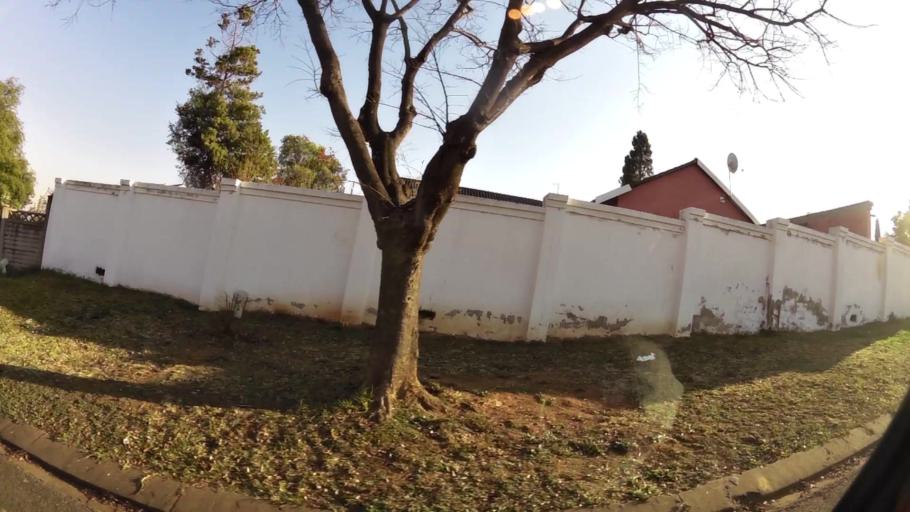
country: ZA
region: Gauteng
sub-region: City of Johannesburg Metropolitan Municipality
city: Soweto
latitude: -26.2909
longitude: 27.9561
